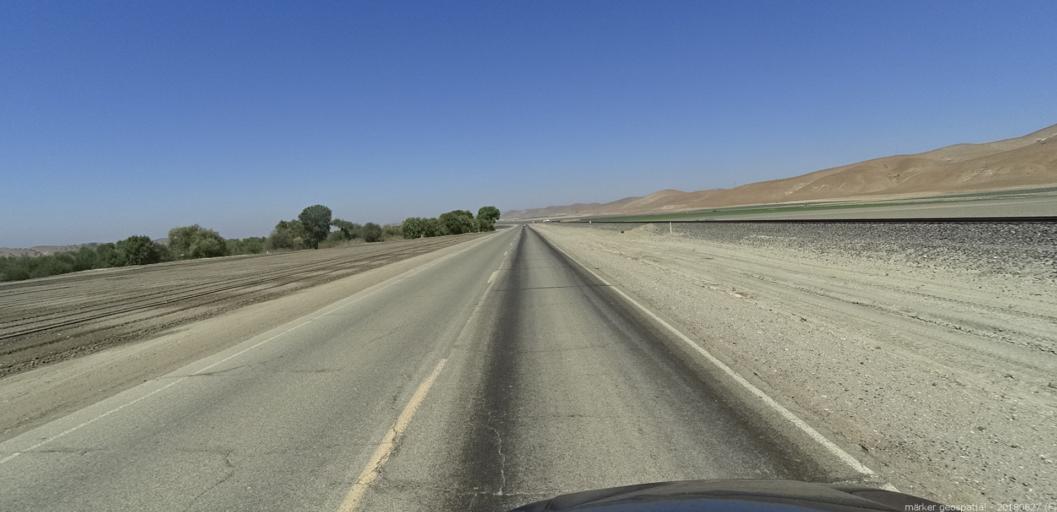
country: US
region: California
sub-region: Monterey County
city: King City
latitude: 36.0524
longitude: -120.9213
